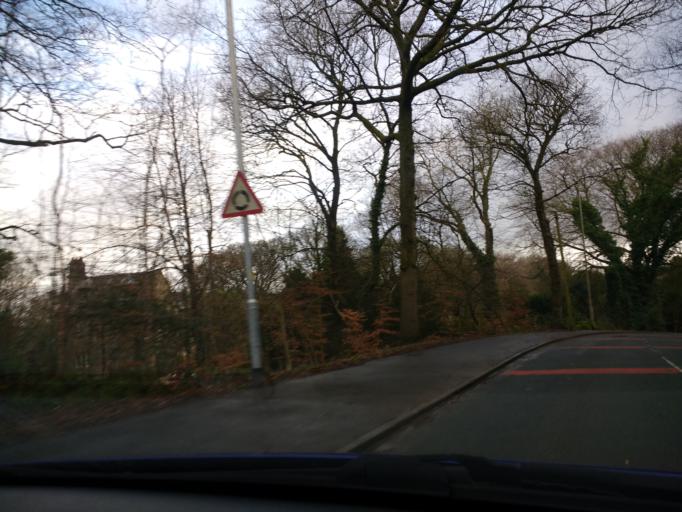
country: GB
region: England
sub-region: Lancashire
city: Lancaster
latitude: 54.0488
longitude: -2.7795
